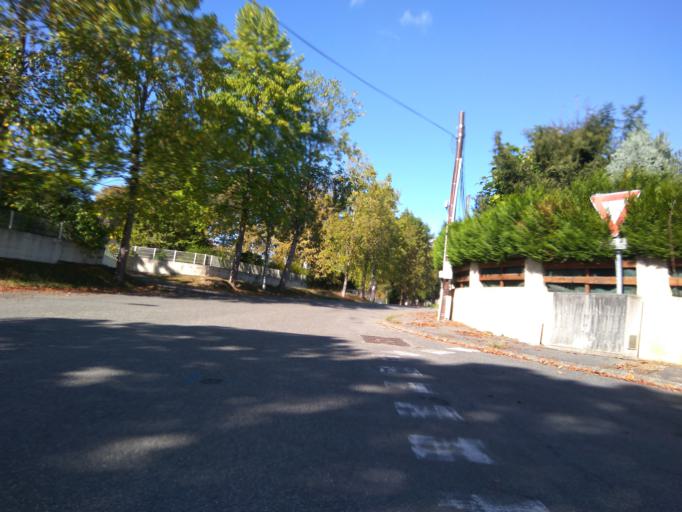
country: FR
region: Aquitaine
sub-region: Departement des Pyrenees-Atlantiques
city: Idron
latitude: 43.2978
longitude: -0.3123
